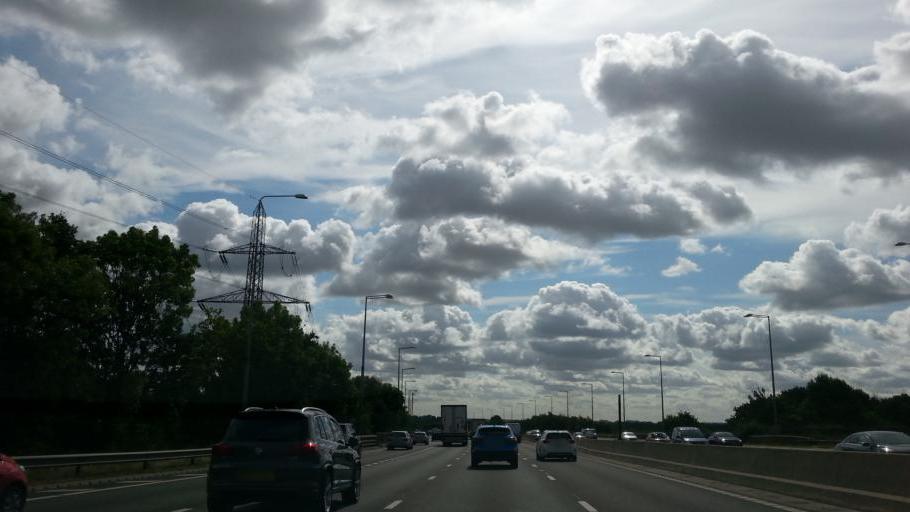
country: GB
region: England
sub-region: Essex
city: Theydon Bois
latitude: 51.6840
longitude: 0.1073
